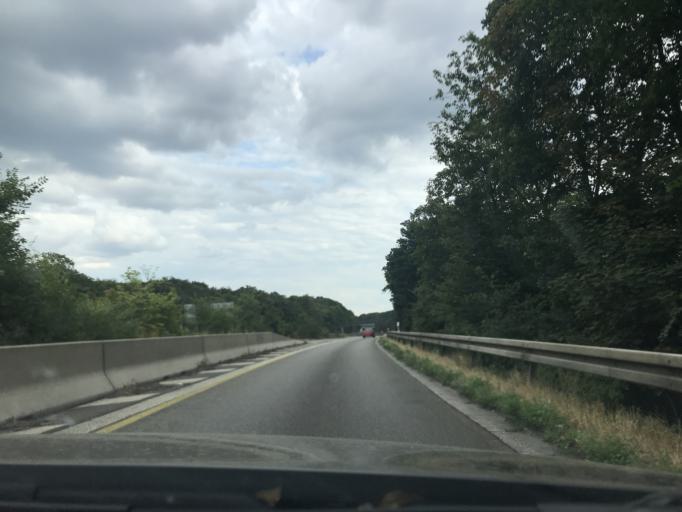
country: DE
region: North Rhine-Westphalia
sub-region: Regierungsbezirk Dusseldorf
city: Erkrath
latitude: 51.1875
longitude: 6.8709
